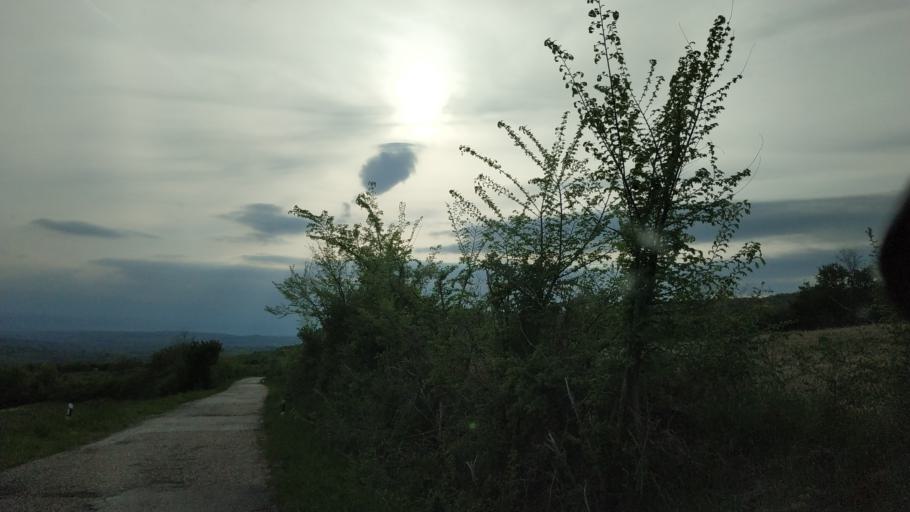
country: RS
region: Central Serbia
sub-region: Zajecarski Okrug
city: Soko Banja
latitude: 43.5307
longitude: 21.8778
